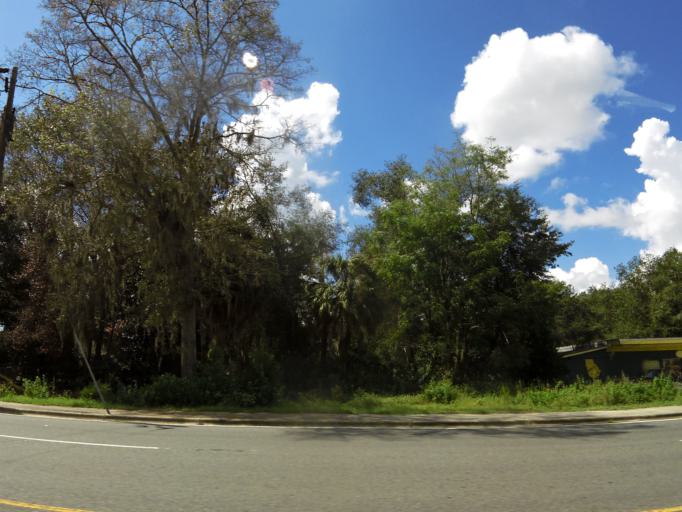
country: US
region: Georgia
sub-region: Charlton County
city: Folkston
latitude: 30.8344
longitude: -82.0070
